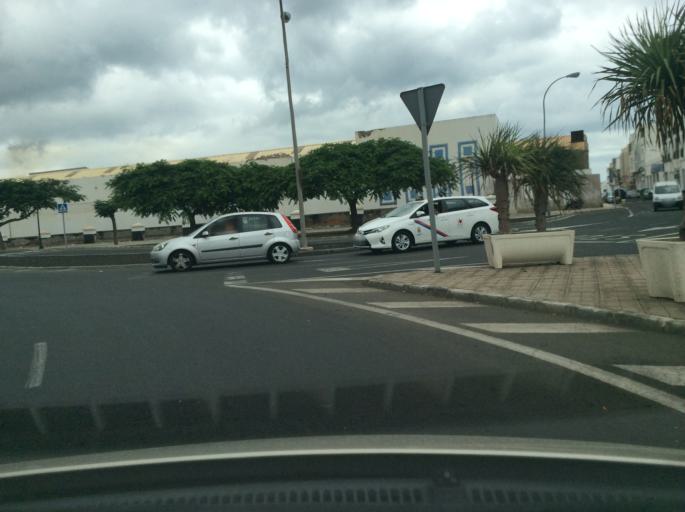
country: ES
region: Canary Islands
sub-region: Provincia de Las Palmas
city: Arrecife
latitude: 28.9671
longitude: -13.5482
